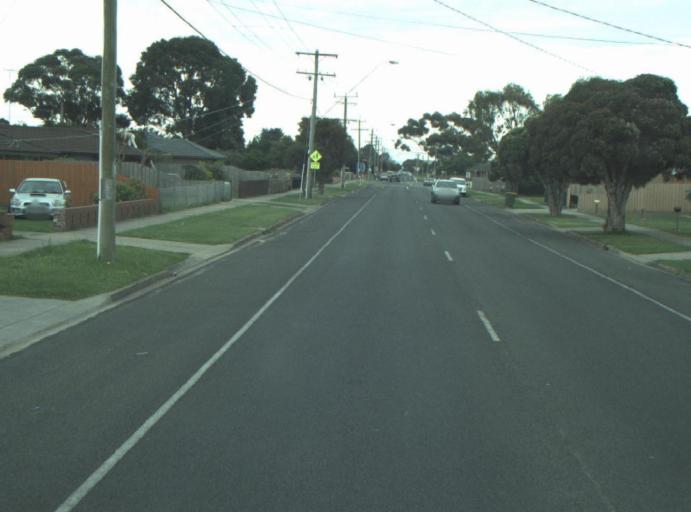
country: AU
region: Victoria
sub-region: Greater Geelong
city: Breakwater
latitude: -38.1775
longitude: 144.3901
